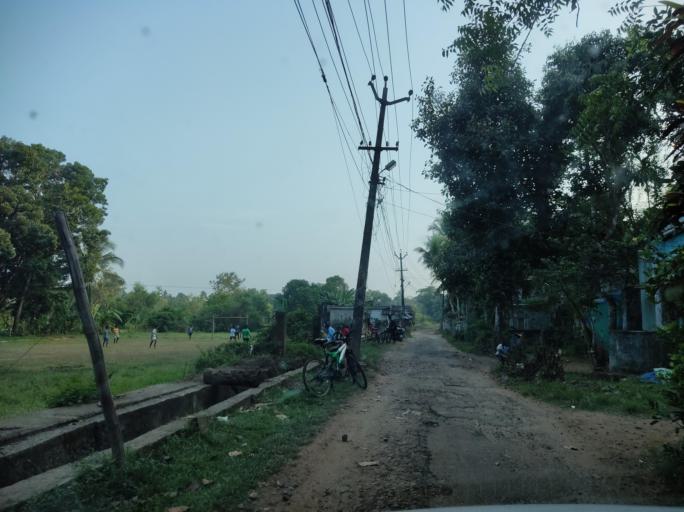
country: IN
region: Kerala
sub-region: Pattanamtitta
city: Tiruvalla
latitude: 9.3640
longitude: 76.5648
